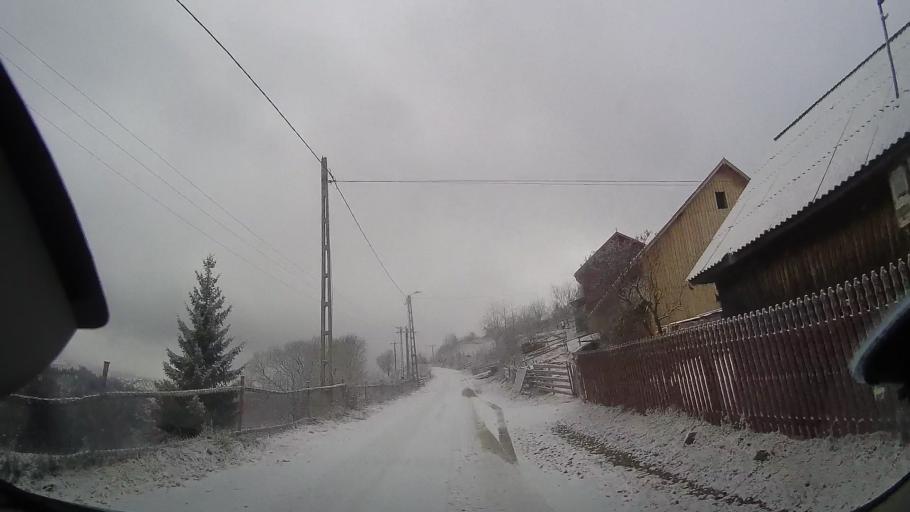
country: RO
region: Cluj
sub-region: Comuna Marisel
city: Marisel
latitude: 46.6611
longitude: 23.1530
